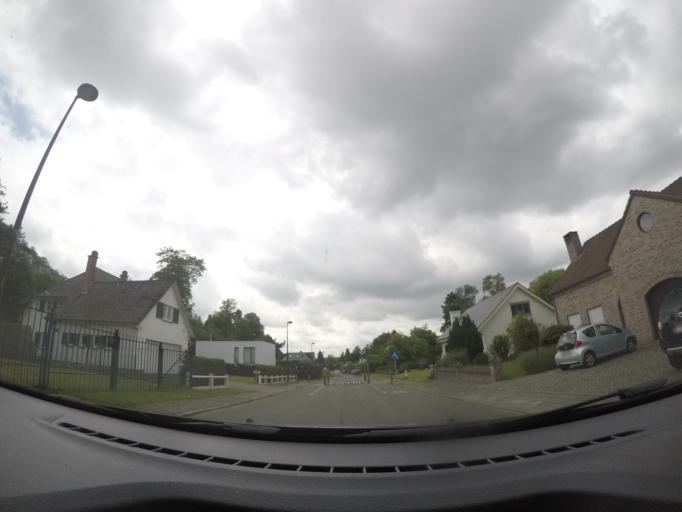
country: BE
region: Flanders
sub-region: Provincie Vlaams-Brabant
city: Sint-Genesius-Rode
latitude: 50.7529
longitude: 4.3471
